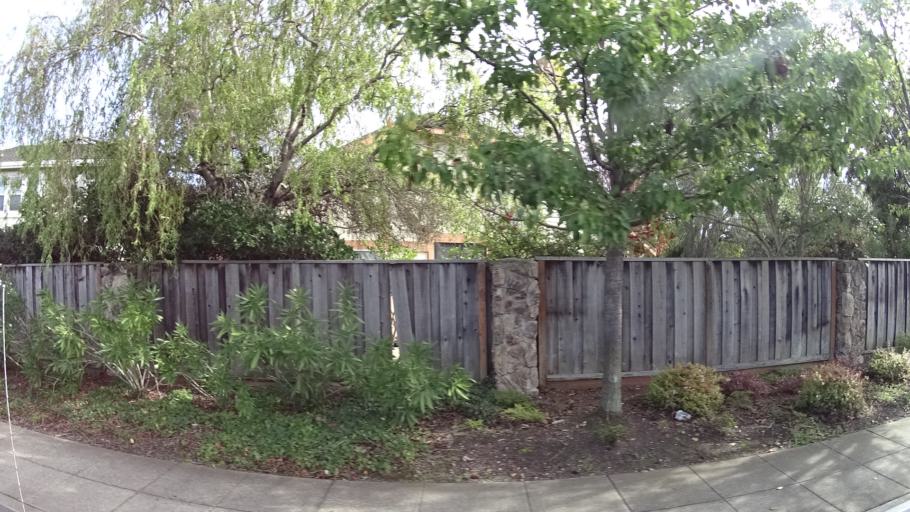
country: US
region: California
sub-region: San Mateo County
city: Belmont
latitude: 37.5386
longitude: -122.2672
